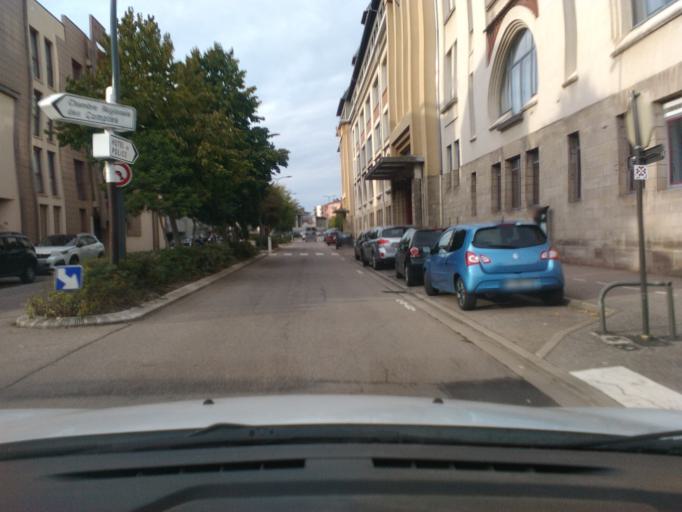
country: FR
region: Lorraine
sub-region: Departement des Vosges
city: Epinal
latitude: 48.1780
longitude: 6.4480
